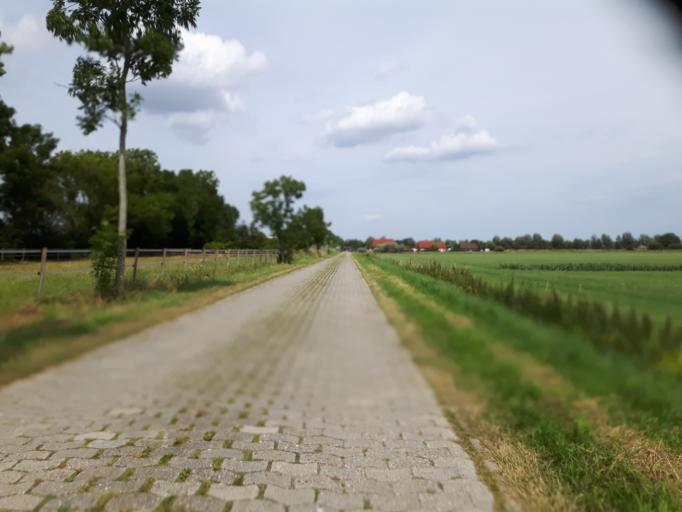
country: DE
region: Lower Saxony
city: Varel
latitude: 53.4040
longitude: 8.1823
